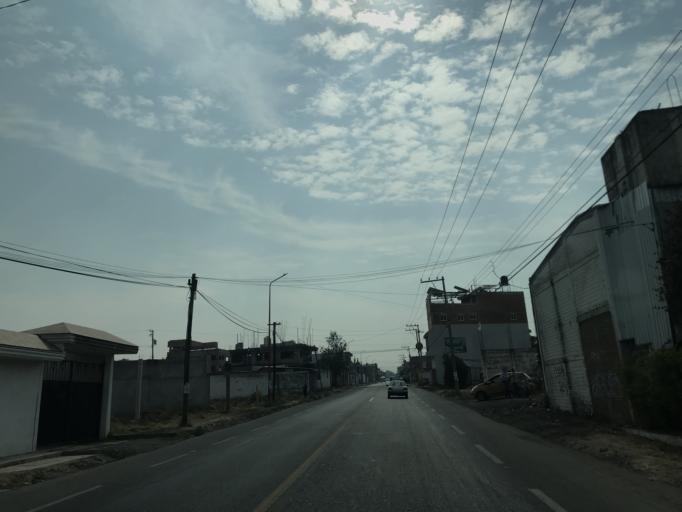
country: MX
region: Tlaxcala
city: Tenancingo
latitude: 19.1511
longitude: -98.2174
